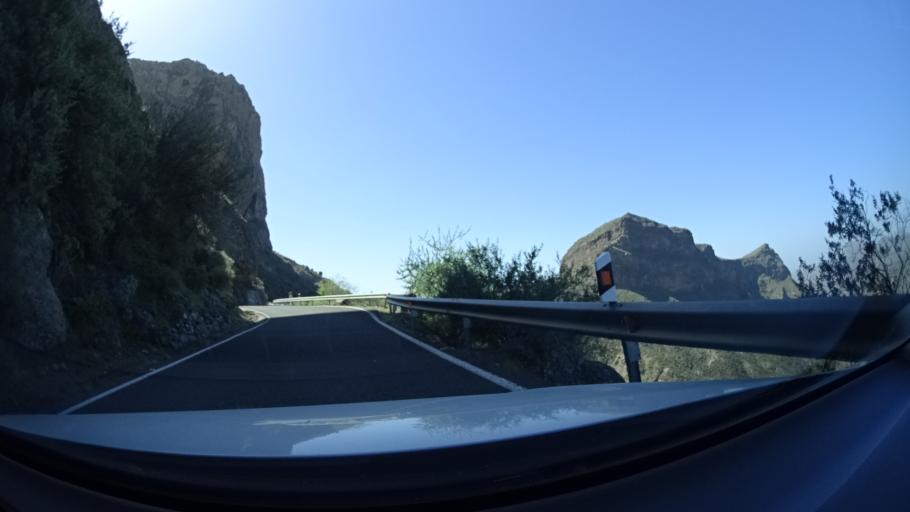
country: ES
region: Canary Islands
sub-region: Provincia de Las Palmas
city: Tejeda
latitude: 27.9661
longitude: -15.6265
